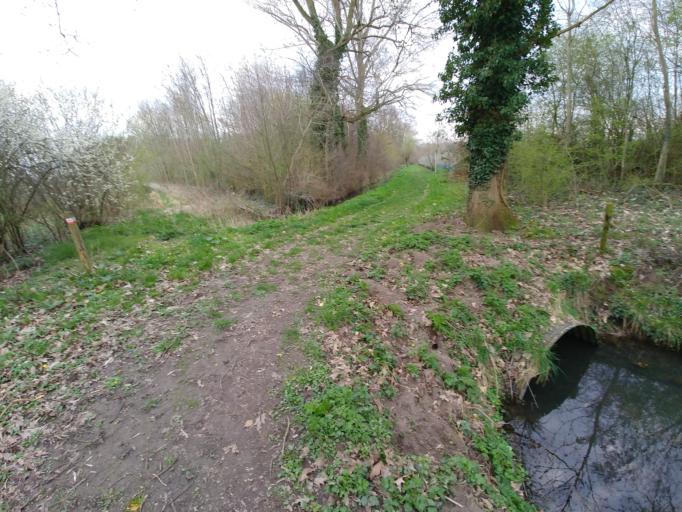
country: NL
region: Gelderland
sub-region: Gemeente Voorst
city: Twello
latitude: 52.2505
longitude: 6.1050
